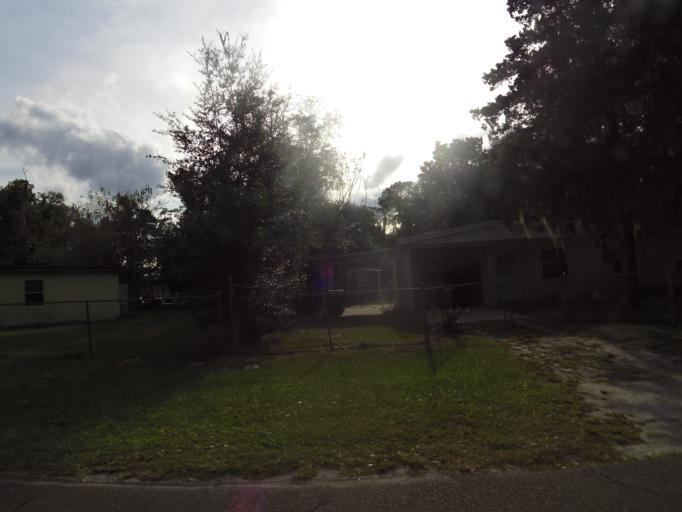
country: US
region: Florida
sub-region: Duval County
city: Jacksonville
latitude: 30.4277
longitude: -81.6734
